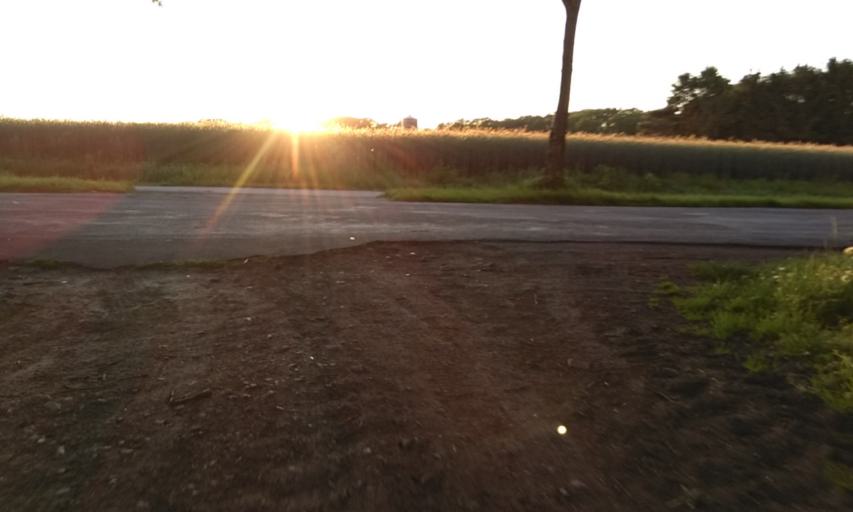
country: DE
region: Lower Saxony
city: Bargstedt
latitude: 53.4377
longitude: 9.4264
